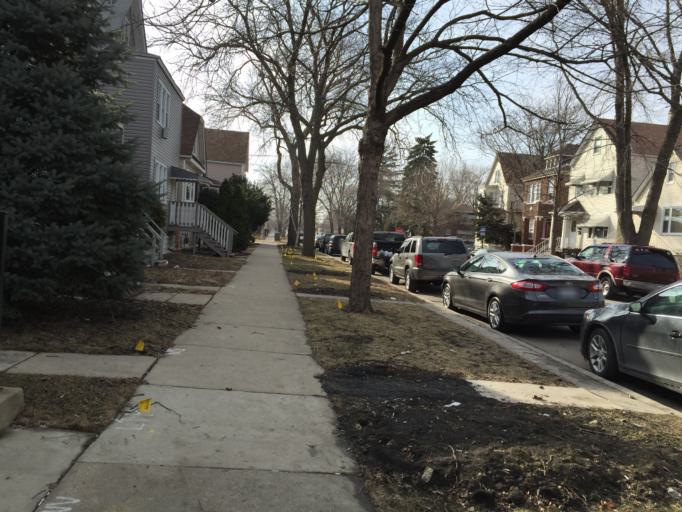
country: US
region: Illinois
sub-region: Cook County
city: Cicero
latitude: 41.8347
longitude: -87.7510
